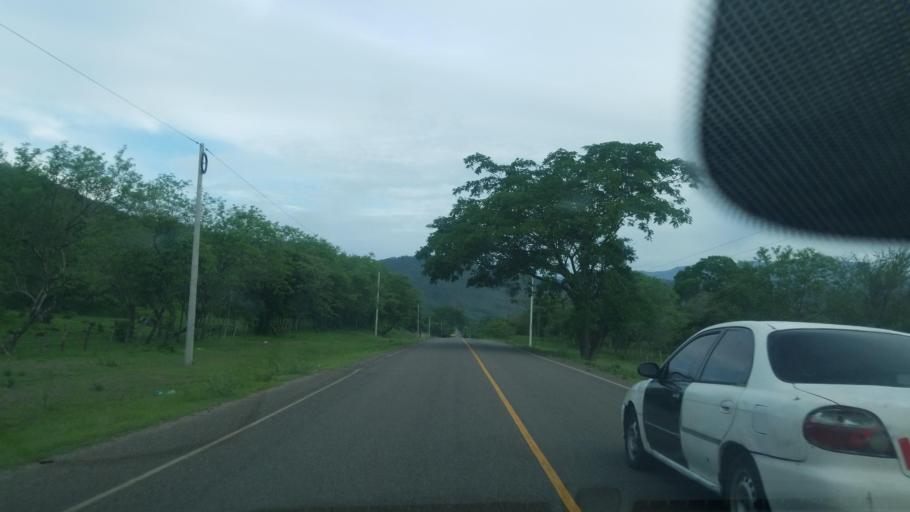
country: HN
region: Santa Barbara
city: San Vicente Centenario
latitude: 14.8686
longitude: -88.2485
